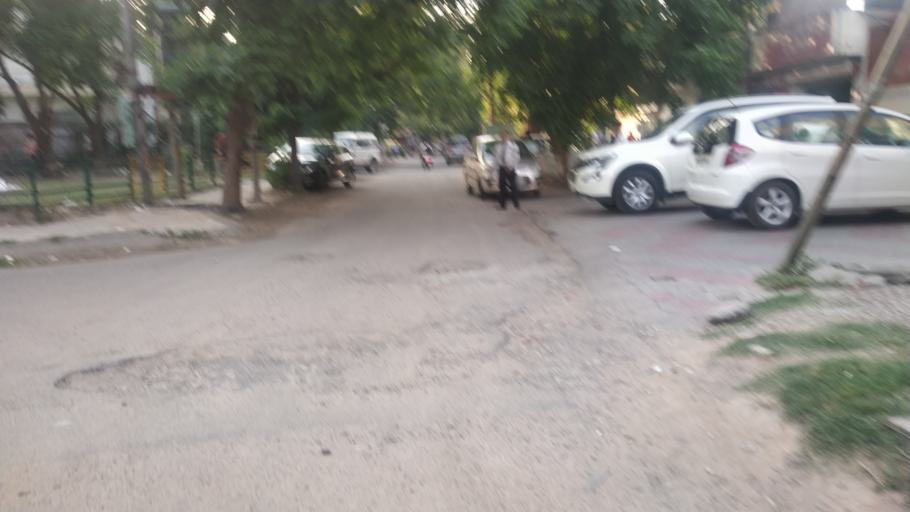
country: IN
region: Punjab
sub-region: Ajitgarh
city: Mohali
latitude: 30.7090
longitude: 76.7222
